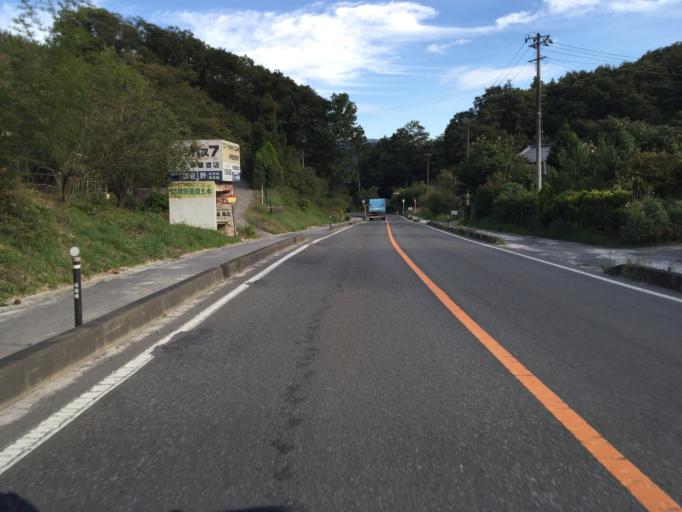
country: JP
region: Fukushima
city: Hobaramachi
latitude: 37.7566
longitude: 140.6001
